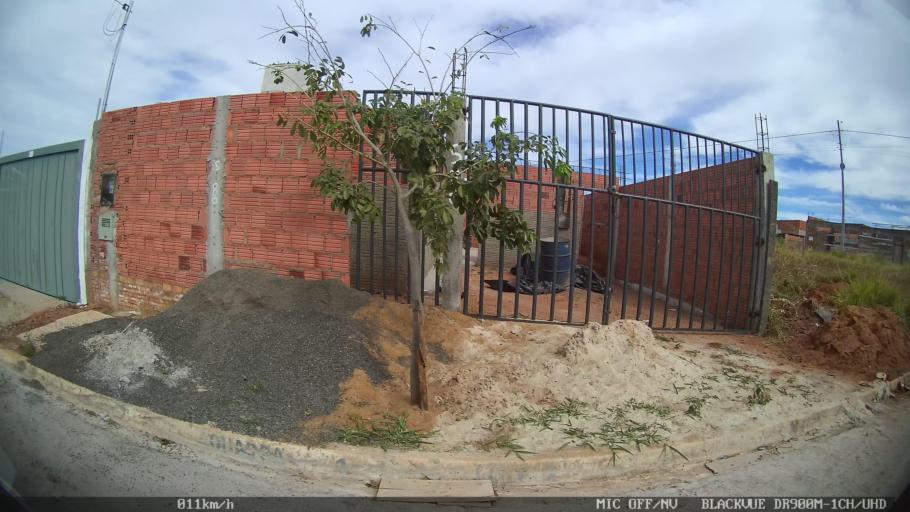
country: BR
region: Sao Paulo
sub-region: Catanduva
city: Catanduva
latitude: -21.1690
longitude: -48.9651
